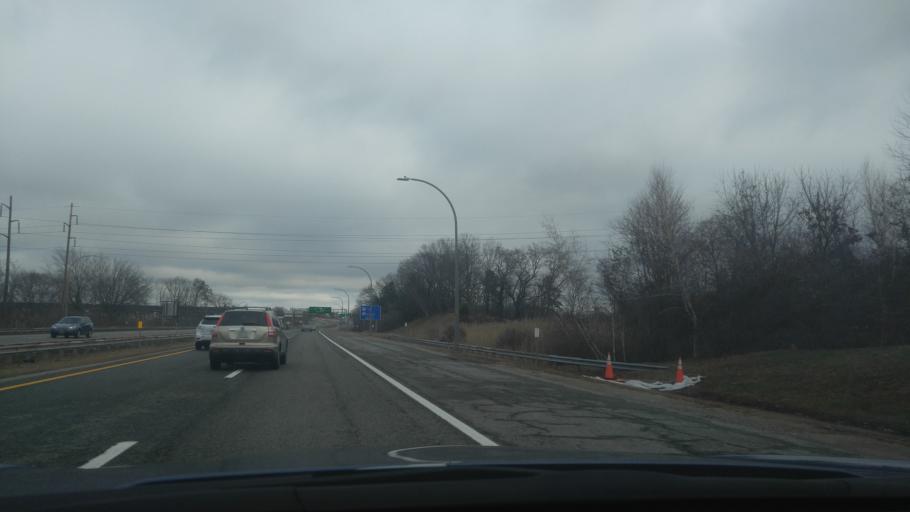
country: US
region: Rhode Island
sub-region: Kent County
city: Warwick
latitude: 41.7266
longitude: -71.4546
